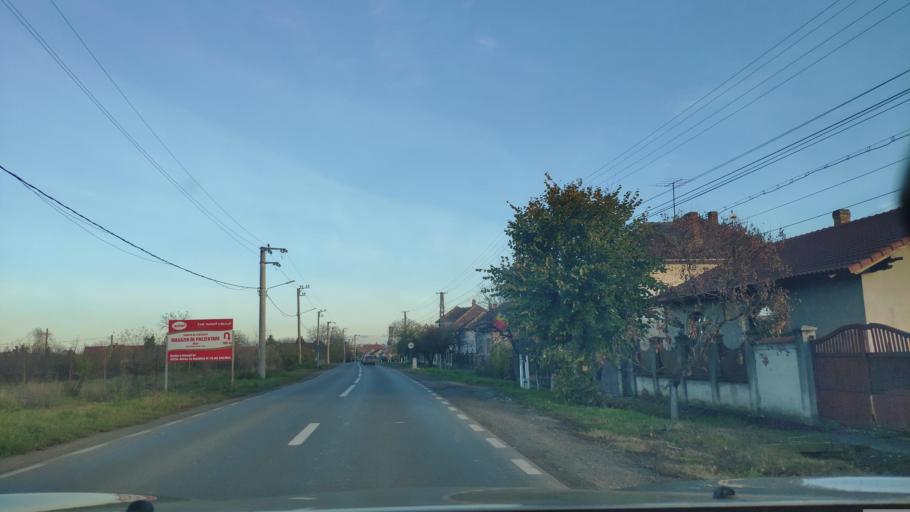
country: RO
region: Satu Mare
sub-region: Comuna Odoreu
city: Odoreu
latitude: 47.7964
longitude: 22.9781
